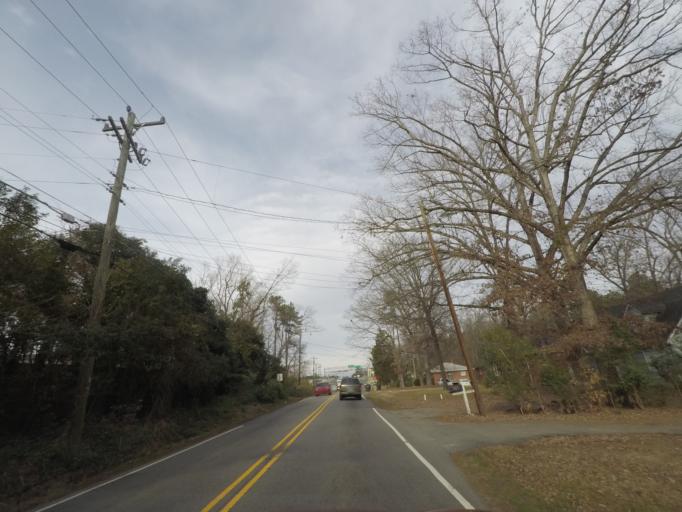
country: US
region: North Carolina
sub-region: Durham County
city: Durham
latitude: 36.0254
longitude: -78.9359
